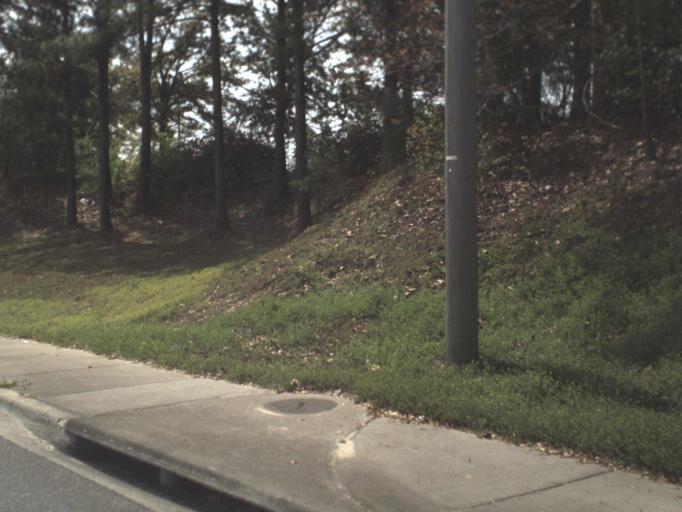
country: US
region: Florida
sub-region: Leon County
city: Tallahassee
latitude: 30.4967
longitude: -84.2464
